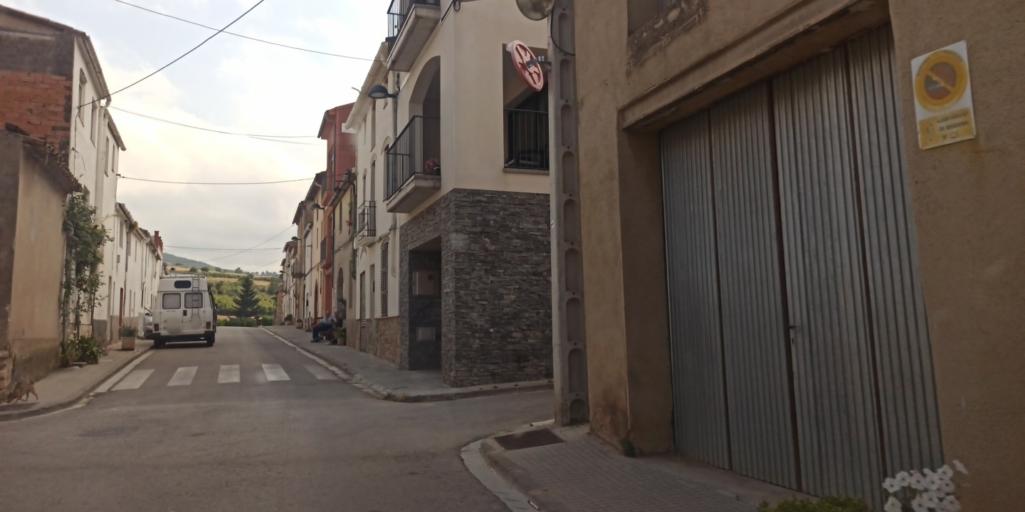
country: ES
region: Catalonia
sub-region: Provincia de Barcelona
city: Sant Joan de Mediona
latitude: 41.4626
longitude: 1.5875
